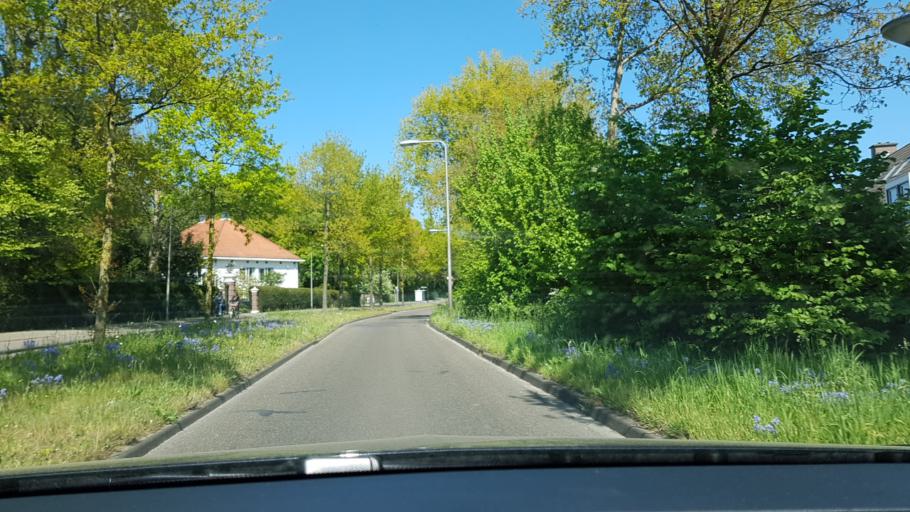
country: NL
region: North Holland
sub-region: Gemeente Heemstede
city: Heemstede
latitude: 52.3350
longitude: 4.6161
